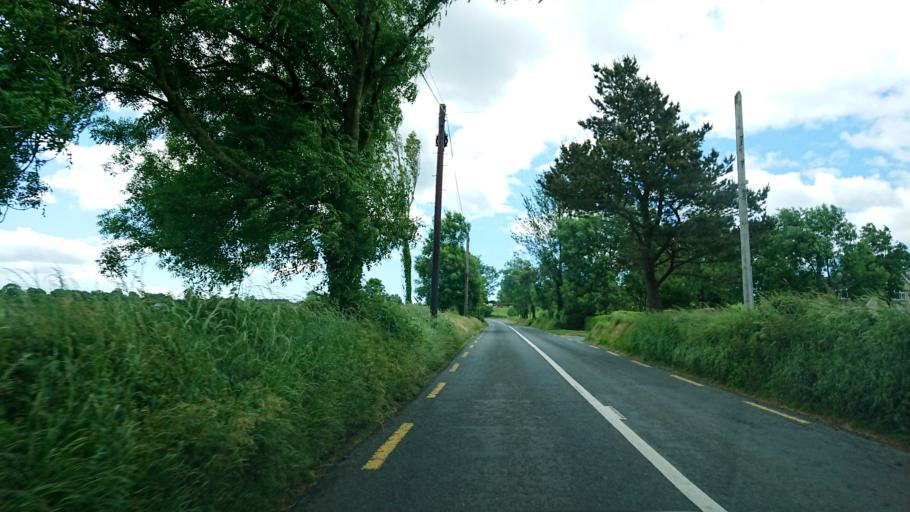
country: IE
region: Munster
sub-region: Waterford
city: Tra Mhor
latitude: 52.2173
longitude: -7.1971
